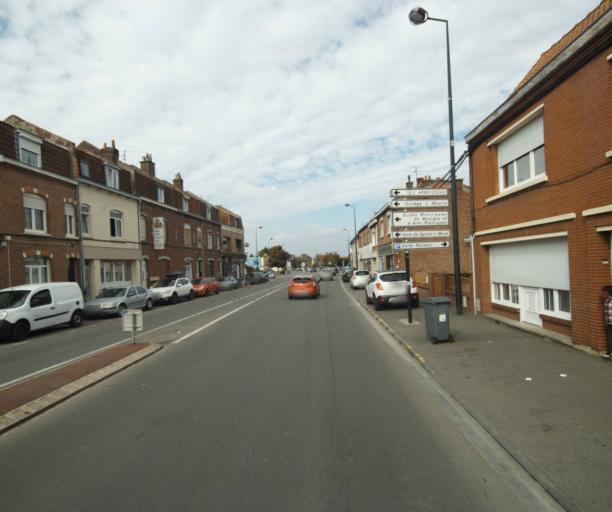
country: FR
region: Nord-Pas-de-Calais
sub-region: Departement du Nord
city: Wattignies
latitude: 50.5959
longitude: 3.0512
